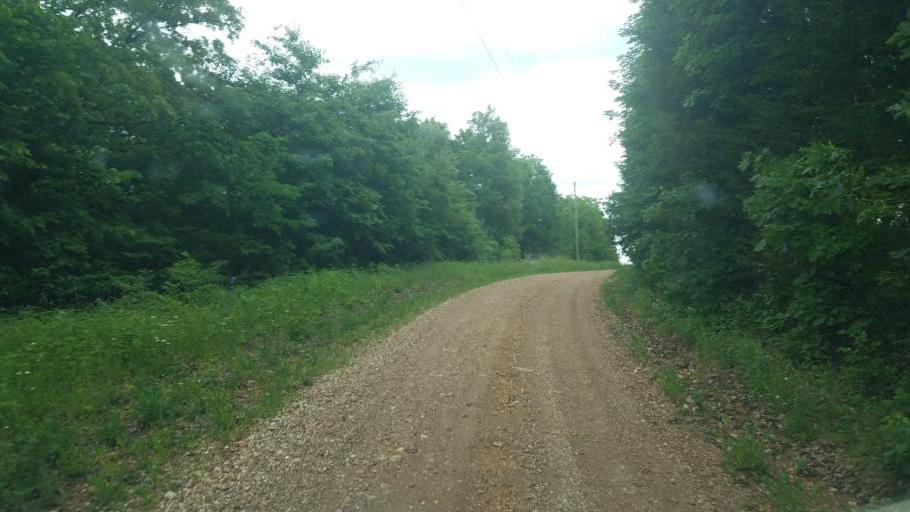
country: US
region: Missouri
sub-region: Moniteau County
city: California
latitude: 38.6125
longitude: -92.6460
